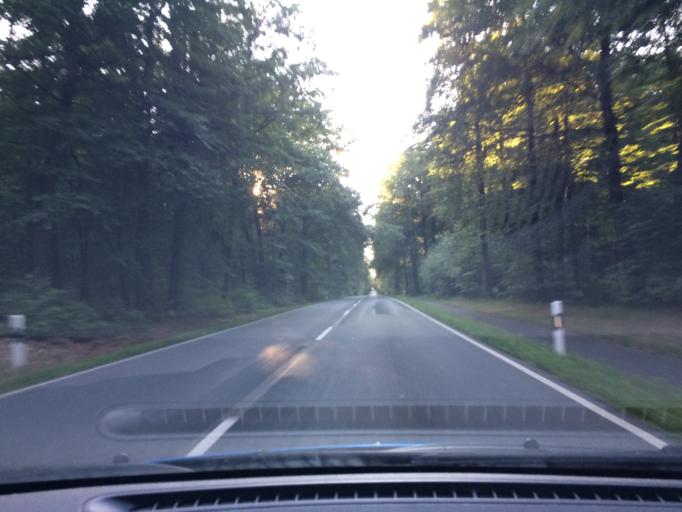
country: DE
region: Lower Saxony
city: Unterluss
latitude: 52.8185
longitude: 10.3369
